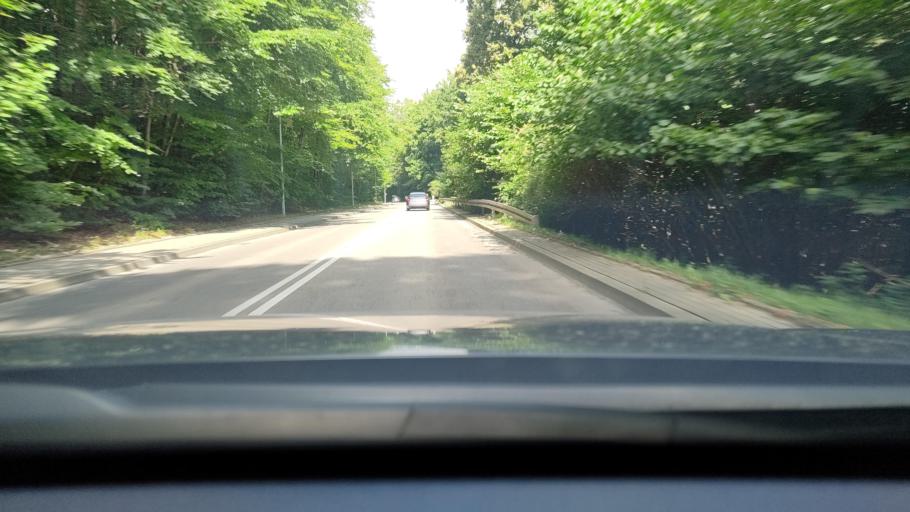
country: PL
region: Pomeranian Voivodeship
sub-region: Powiat wejherowski
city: Wejherowo
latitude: 54.5938
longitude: 18.2357
